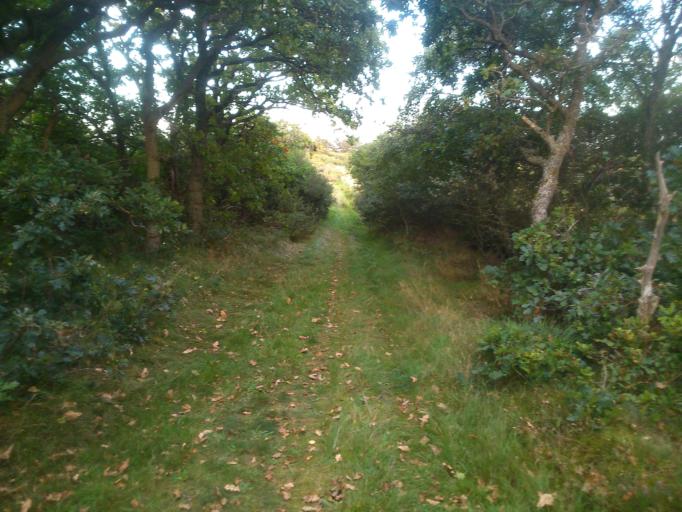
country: DK
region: South Denmark
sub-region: Varde Kommune
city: Oksbol
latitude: 55.6907
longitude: 8.1869
